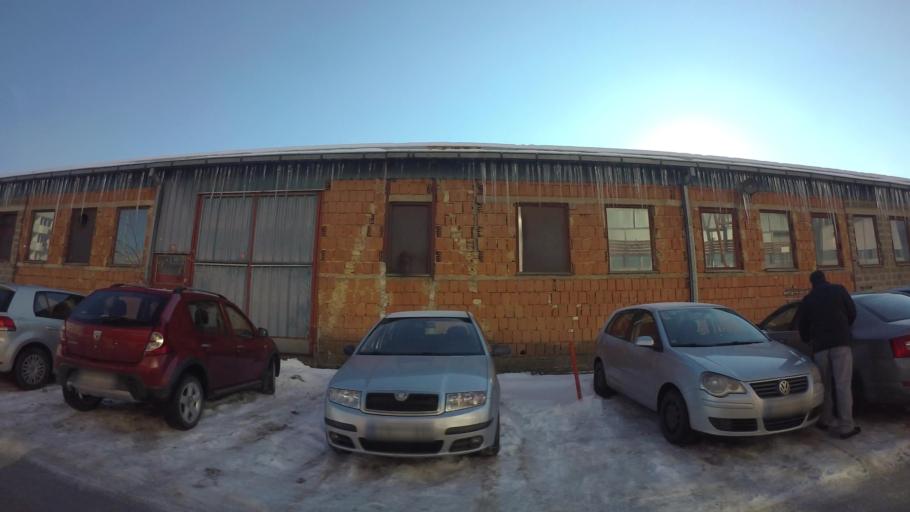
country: BA
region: Federation of Bosnia and Herzegovina
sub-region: Kanton Sarajevo
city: Sarajevo
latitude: 43.8264
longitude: 18.3680
